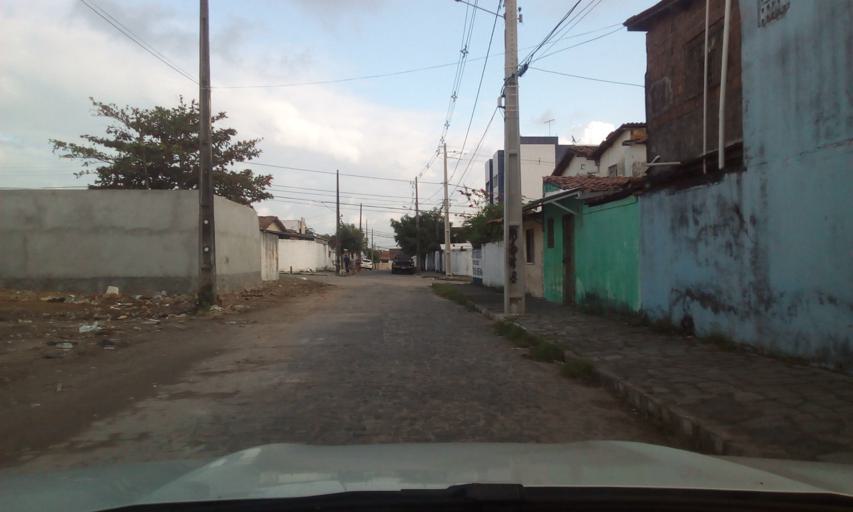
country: BR
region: Paraiba
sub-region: Joao Pessoa
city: Joao Pessoa
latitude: -7.1680
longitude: -34.8432
